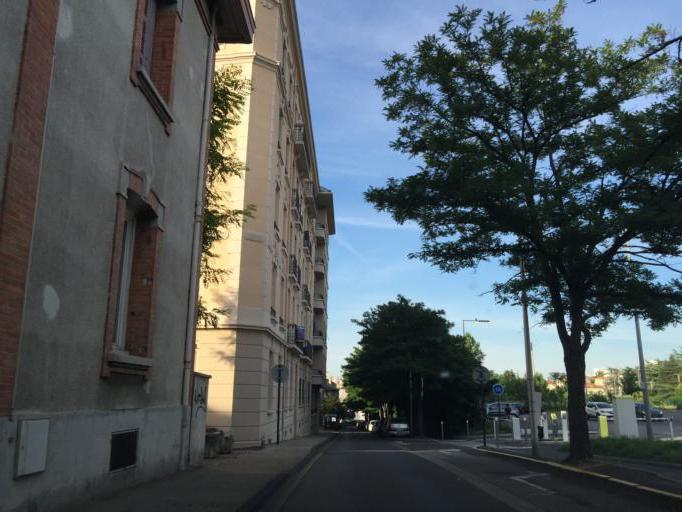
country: FR
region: Rhone-Alpes
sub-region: Departement de la Loire
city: Saint-Chamond
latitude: 45.4738
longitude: 4.5180
